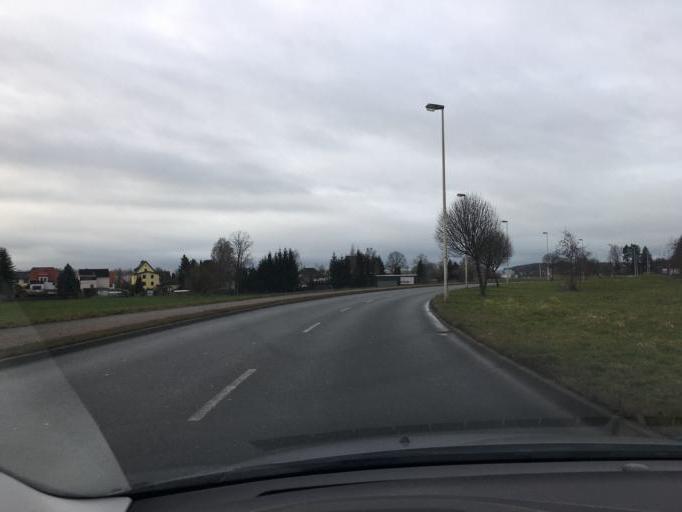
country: DE
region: Saxony
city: Glauchau
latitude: 50.8391
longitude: 12.5370
